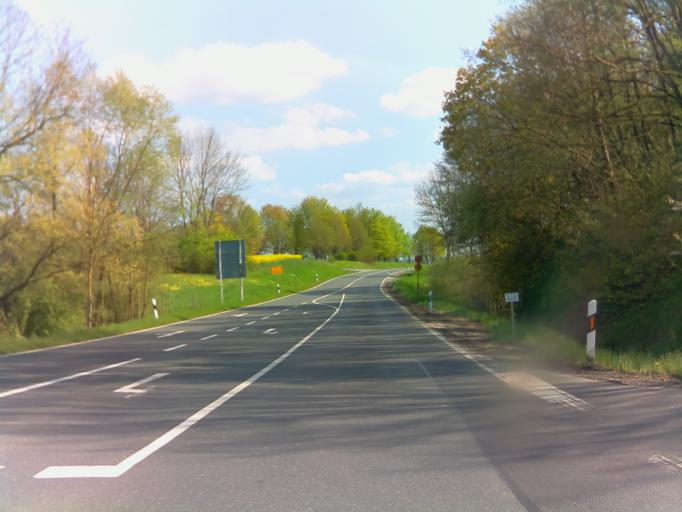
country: DE
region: Thuringia
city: Veilsdorf
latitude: 50.3372
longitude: 10.7916
